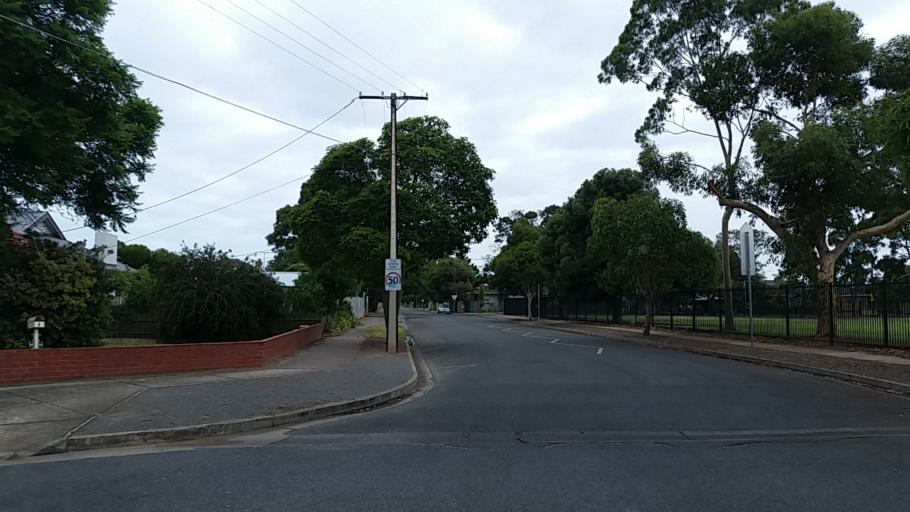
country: AU
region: South Australia
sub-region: Holdfast Bay
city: North Brighton
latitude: -35.0029
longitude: 138.5246
